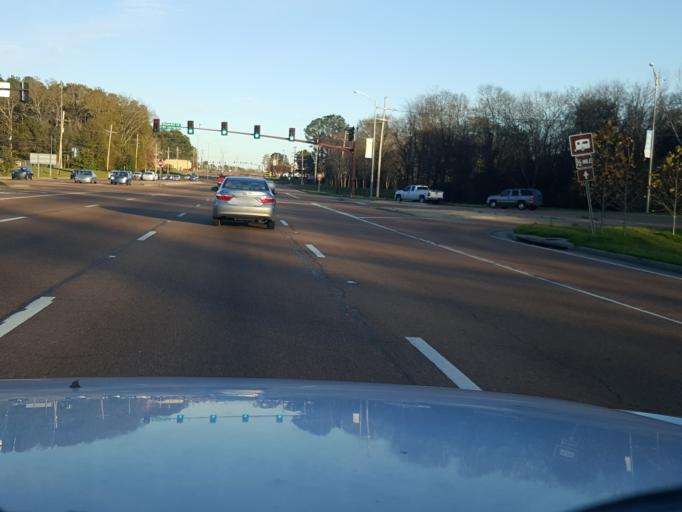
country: US
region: Mississippi
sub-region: Rankin County
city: Flowood
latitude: 32.3339
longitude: -90.1568
